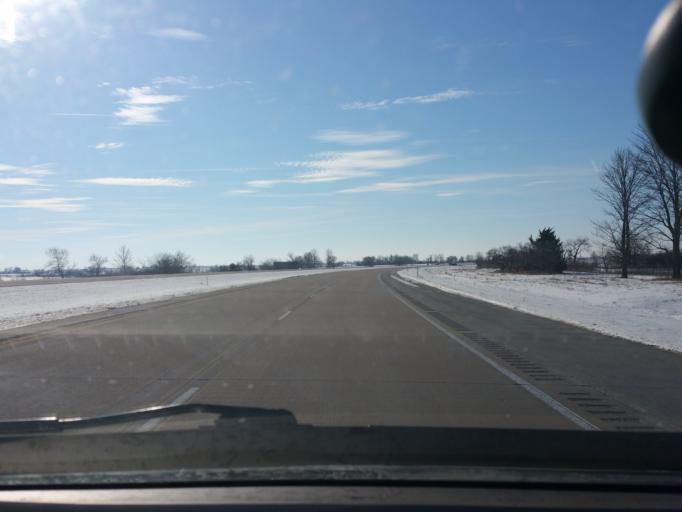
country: US
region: Iowa
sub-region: Decatur County
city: Leon
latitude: 40.8461
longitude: -93.8045
